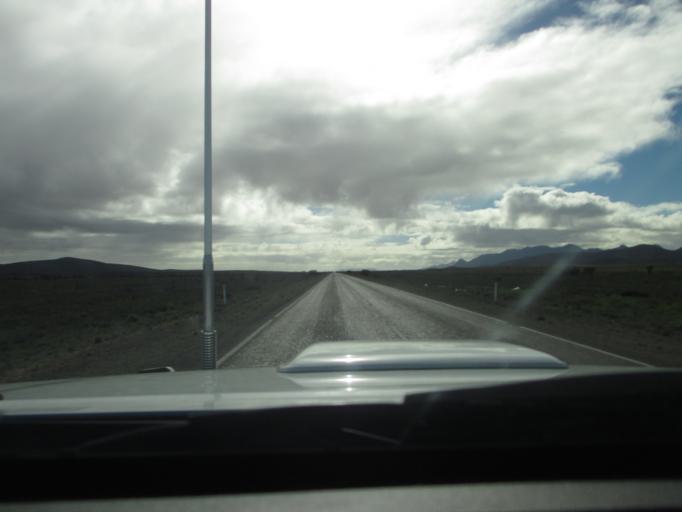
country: AU
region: South Australia
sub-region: Flinders Ranges
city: Quorn
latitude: -31.6539
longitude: 138.3783
